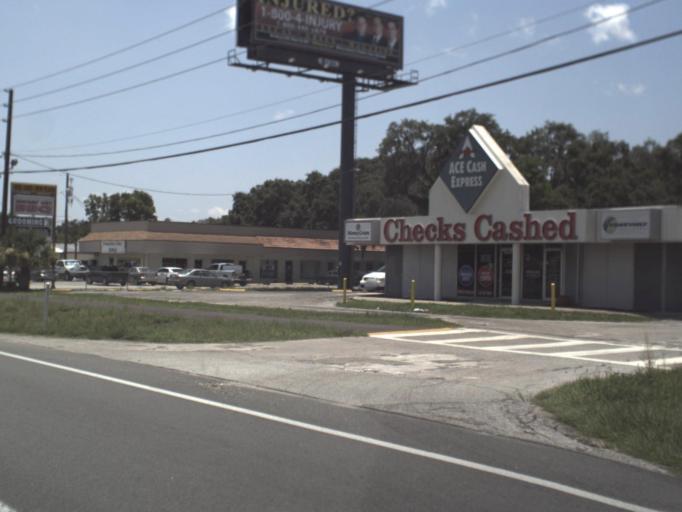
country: US
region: Florida
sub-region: Pasco County
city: Beacon Square
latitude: 28.2083
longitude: -82.7398
